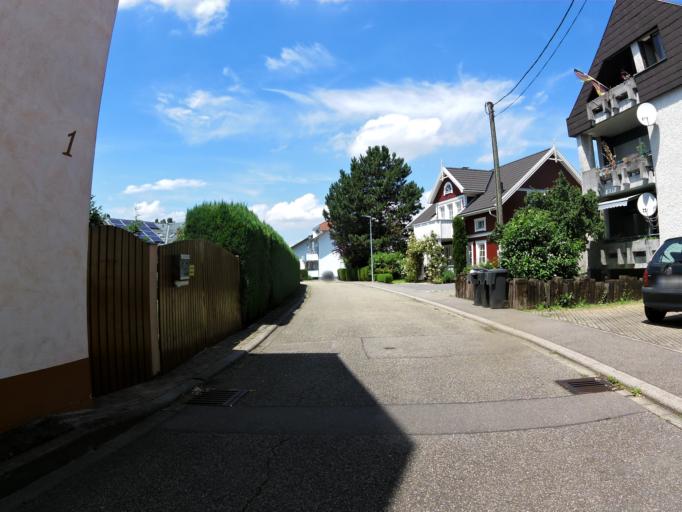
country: DE
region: Baden-Wuerttemberg
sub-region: Freiburg Region
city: Kippenheim
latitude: 48.3175
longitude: 7.8047
